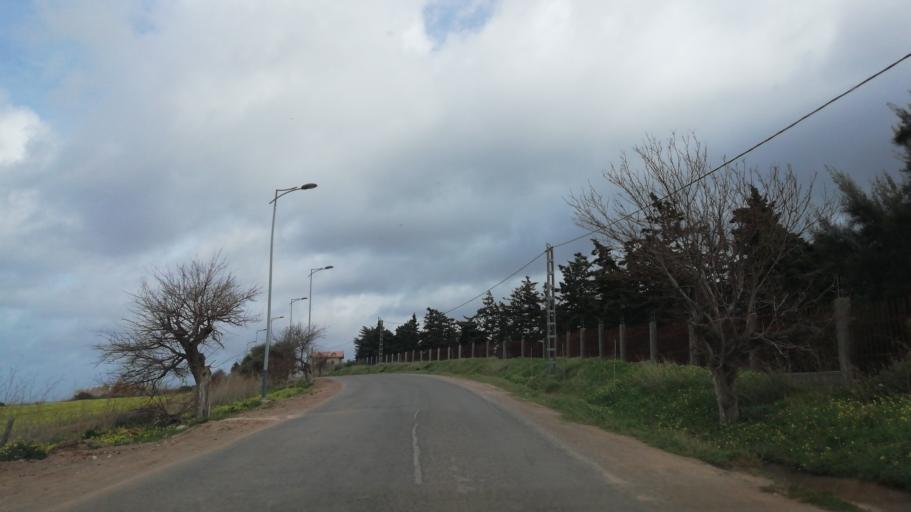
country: DZ
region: Oran
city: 'Ain el Turk
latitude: 35.6909
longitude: -0.8622
